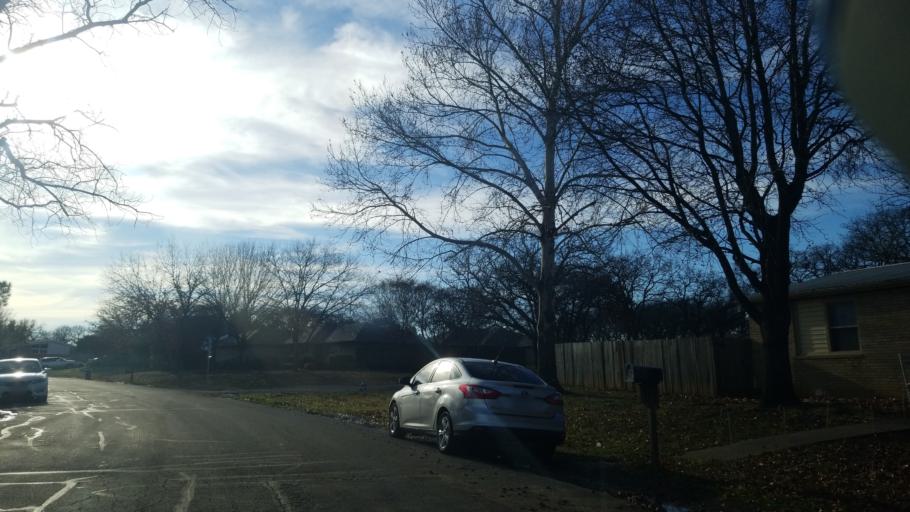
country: US
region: Texas
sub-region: Denton County
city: Corinth
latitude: 33.1392
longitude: -97.0633
